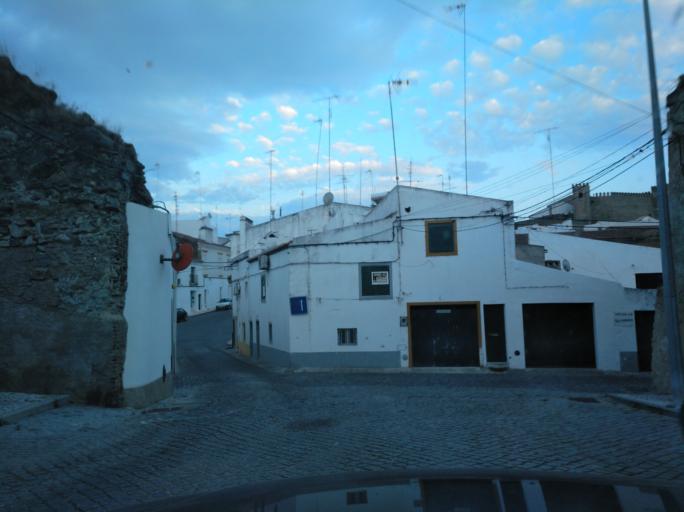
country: PT
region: Portalegre
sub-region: Campo Maior
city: Campo Maior
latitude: 39.0136
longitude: -7.0733
